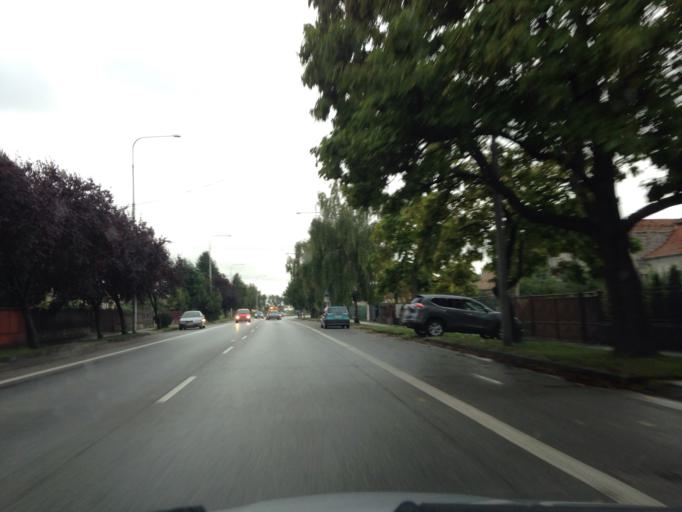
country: SK
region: Nitriansky
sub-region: Okres Komarno
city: Hurbanovo
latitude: 47.8635
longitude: 18.1856
